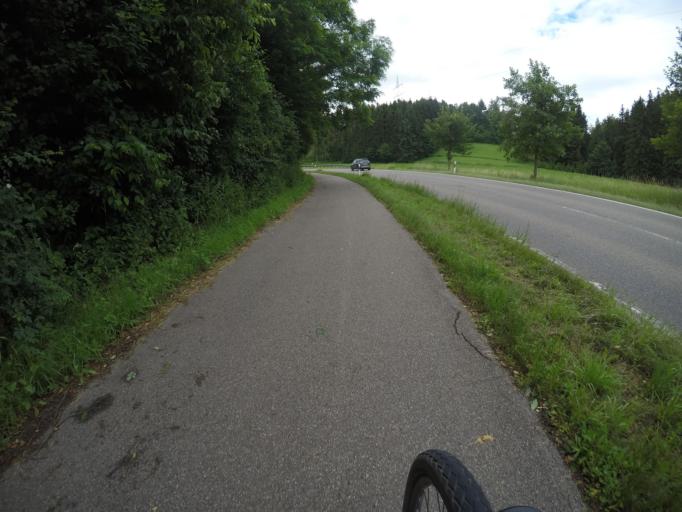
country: DE
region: Baden-Wuerttemberg
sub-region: Regierungsbezirk Stuttgart
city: Gartringen
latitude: 48.6536
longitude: 8.8823
